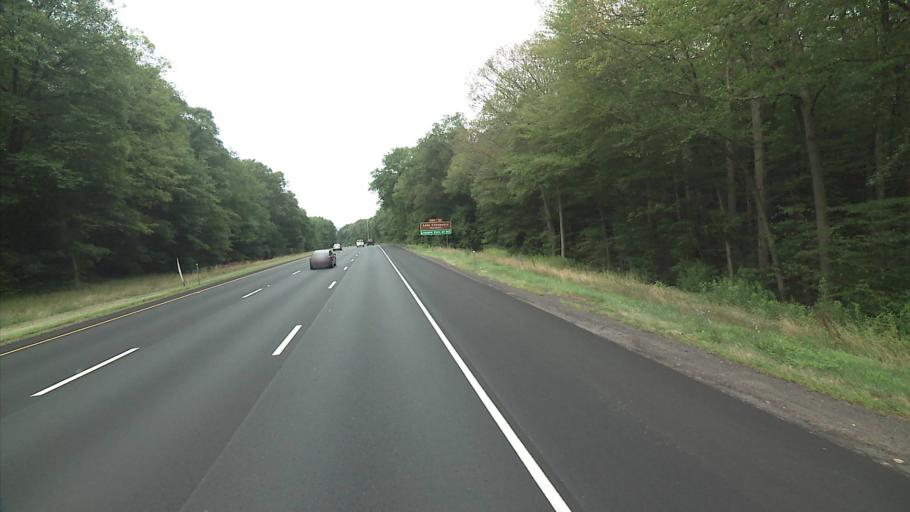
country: US
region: Connecticut
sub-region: Hartford County
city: Plainville
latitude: 41.6234
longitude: -72.8877
